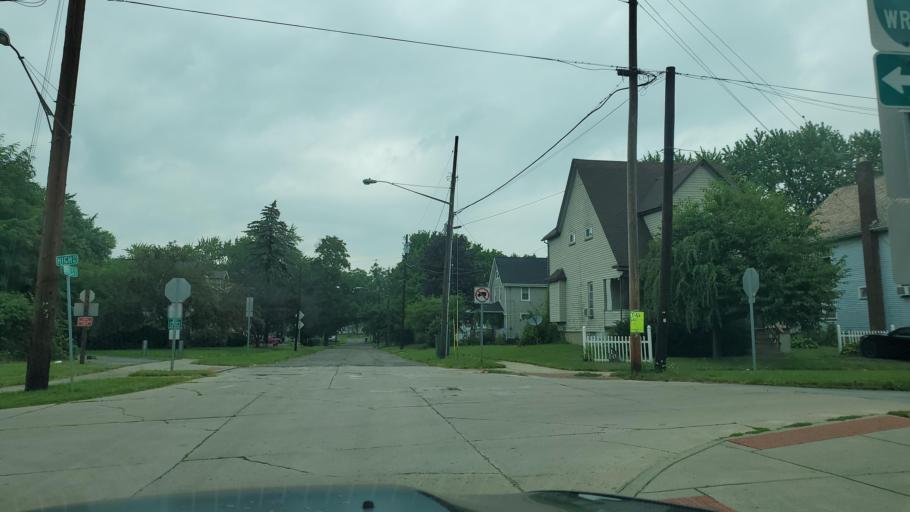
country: US
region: Ohio
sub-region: Trumbull County
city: Warren
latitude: 41.2377
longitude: -80.8044
